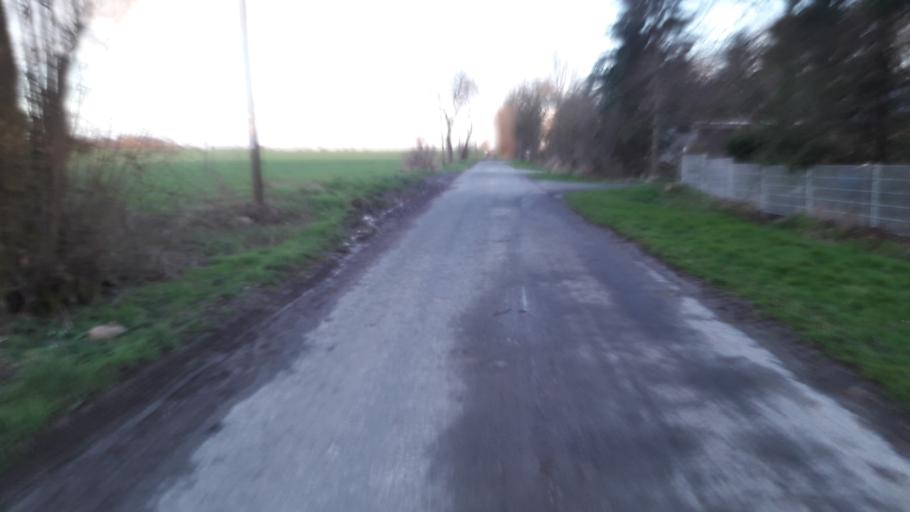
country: DE
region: North Rhine-Westphalia
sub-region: Regierungsbezirk Detmold
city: Paderborn
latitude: 51.6933
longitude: 8.7735
